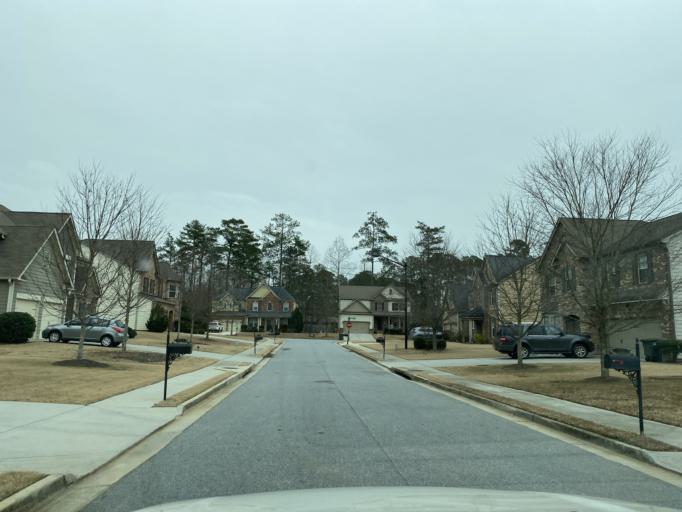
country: US
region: Georgia
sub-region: Cobb County
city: Fair Oaks
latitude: 33.9143
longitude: -84.5741
